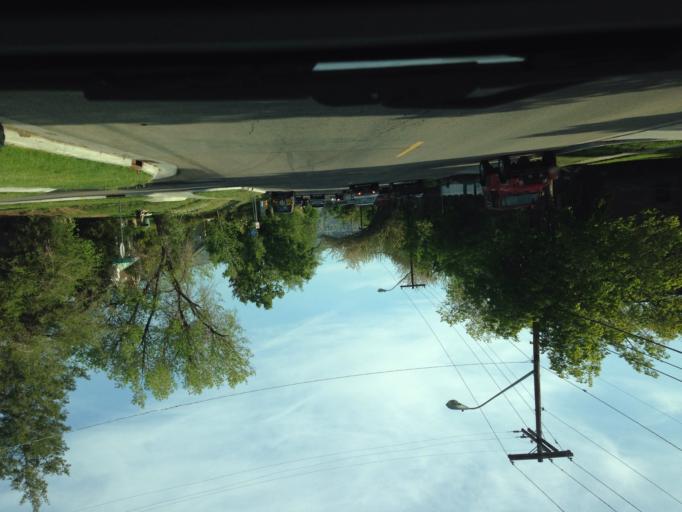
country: US
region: Utah
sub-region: Salt Lake County
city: Salt Lake City
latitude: 40.7461
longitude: -111.8653
